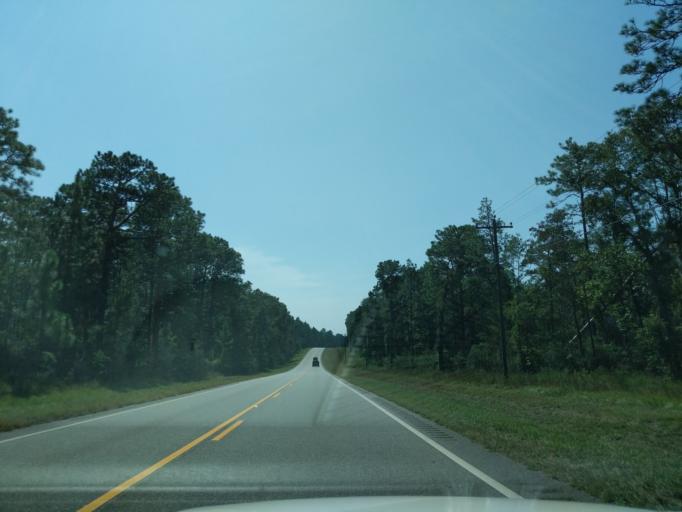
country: US
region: Alabama
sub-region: Covington County
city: Andalusia
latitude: 31.2177
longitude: -86.5354
